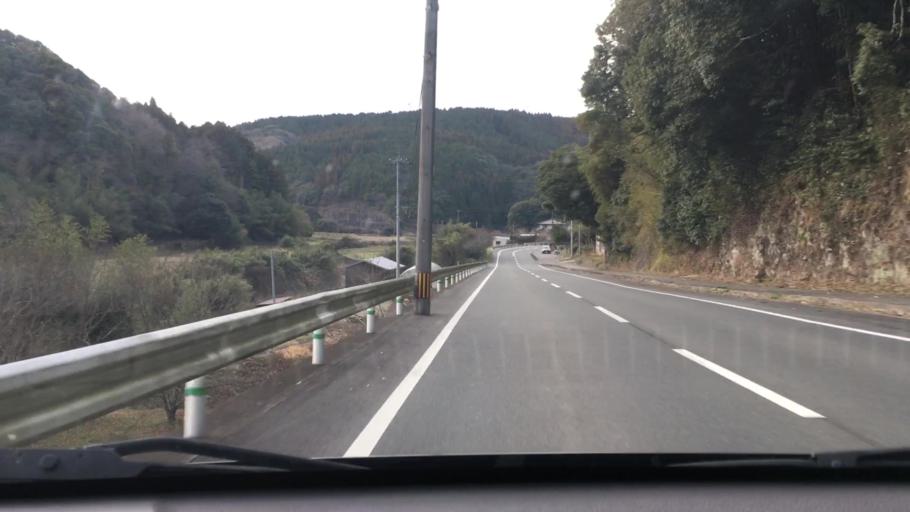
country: JP
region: Oita
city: Hiji
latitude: 33.4211
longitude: 131.4181
